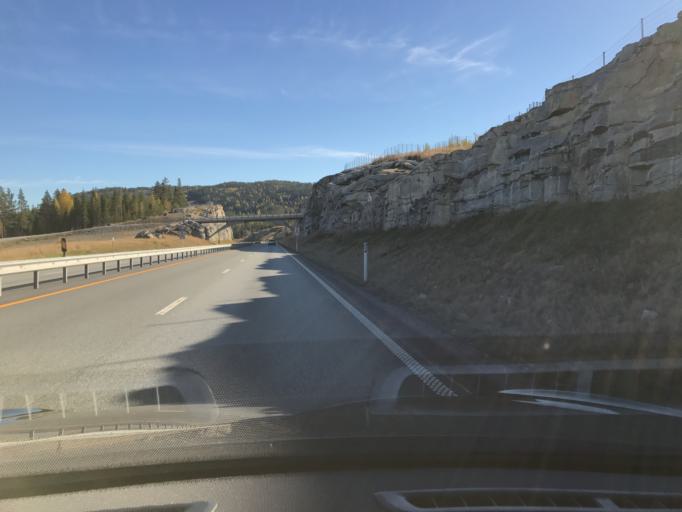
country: NO
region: Buskerud
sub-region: Krodsherad
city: Noresund
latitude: 60.2710
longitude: 9.7796
